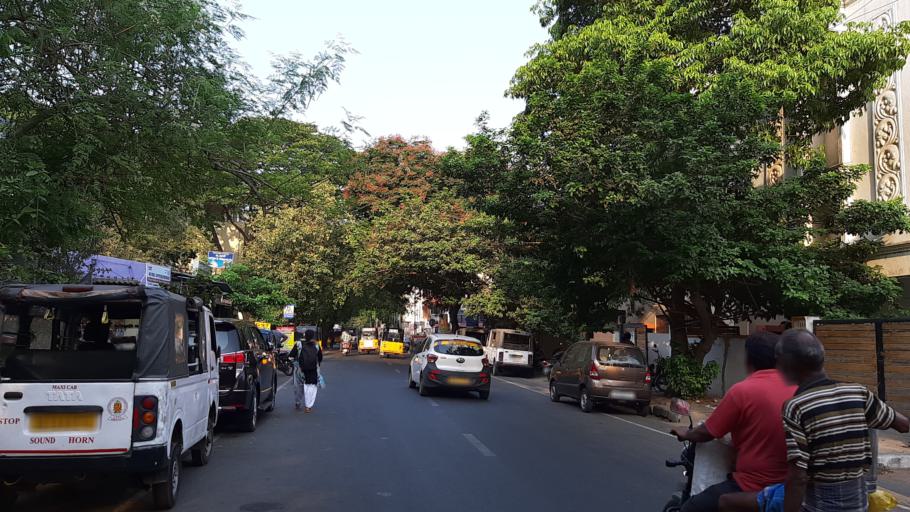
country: IN
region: Tamil Nadu
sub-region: Chennai
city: Gandhi Nagar
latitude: 13.0347
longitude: 80.2325
